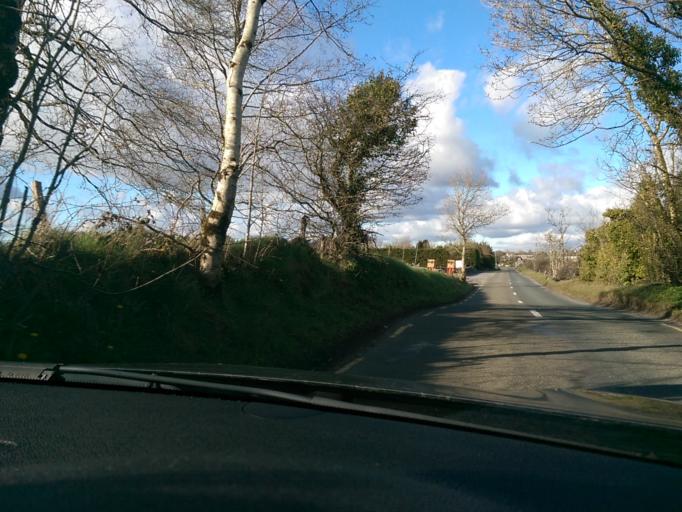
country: IE
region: Connaught
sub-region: Roscommon
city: Castlerea
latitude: 53.5961
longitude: -8.5641
